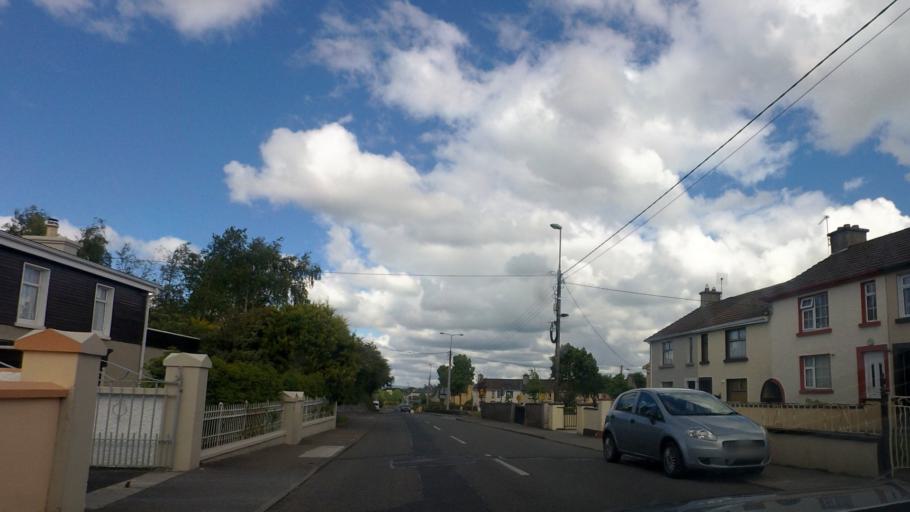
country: IE
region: Munster
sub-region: An Clar
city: Ennis
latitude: 52.8448
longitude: -8.9949
